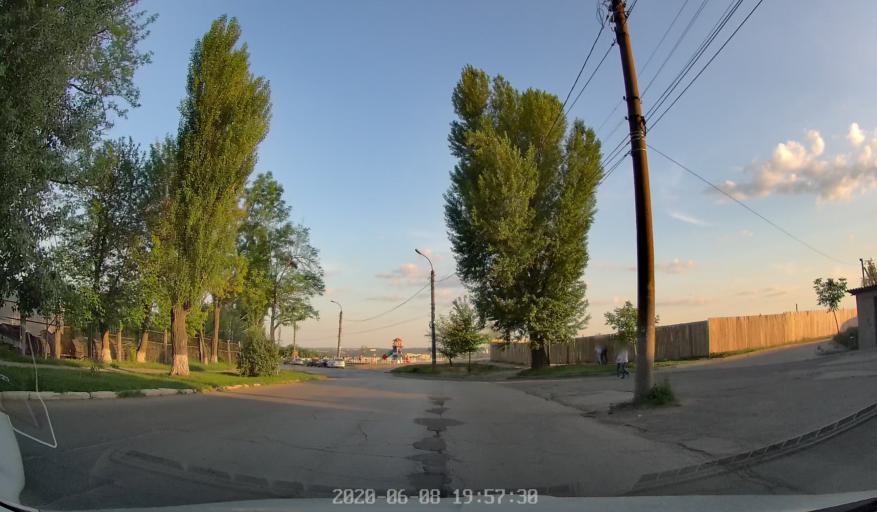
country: MD
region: Chisinau
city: Chisinau
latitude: 47.0155
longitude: 28.8824
